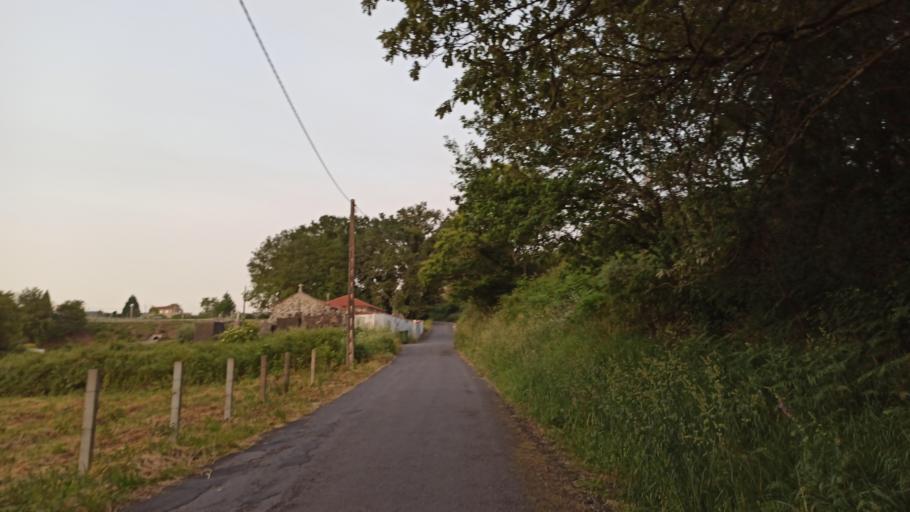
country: ES
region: Galicia
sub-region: Provincia da Coruna
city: Negreira
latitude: 42.9186
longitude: -8.7495
